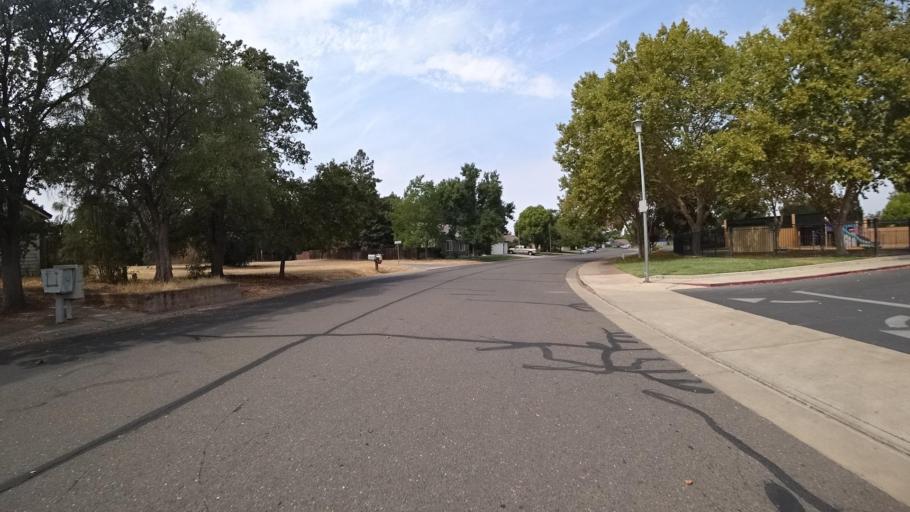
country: US
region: California
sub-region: Sacramento County
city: Elk Grove
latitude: 38.4167
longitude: -121.3871
